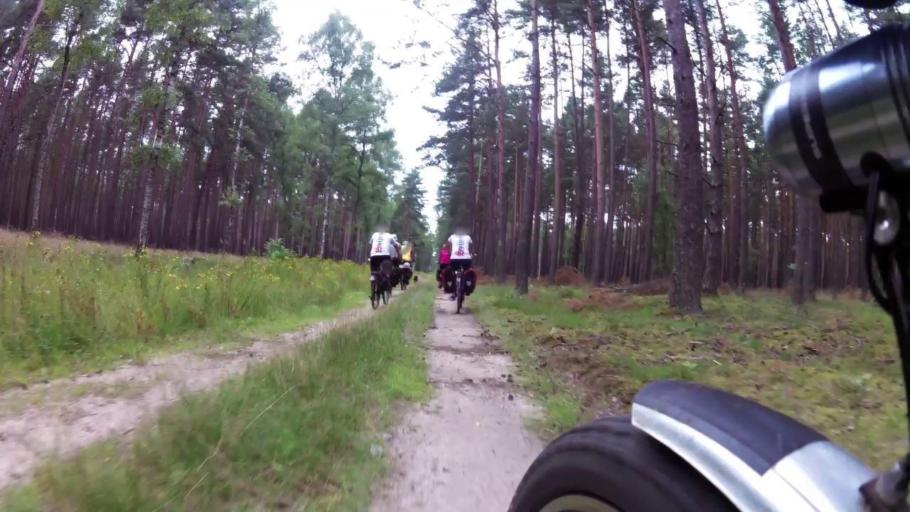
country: PL
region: West Pomeranian Voivodeship
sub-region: Powiat mysliborski
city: Debno
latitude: 52.8305
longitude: 14.6301
